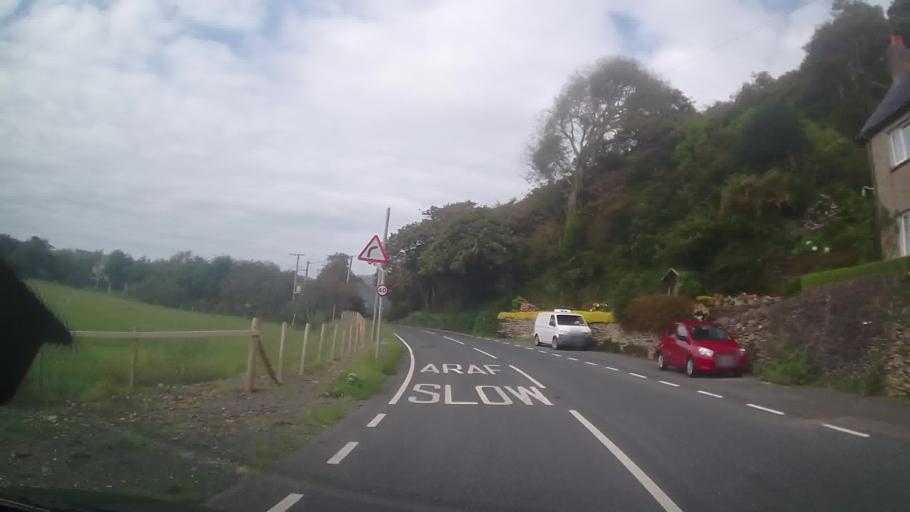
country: GB
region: Wales
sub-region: Gwynedd
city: Barmouth
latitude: 52.6966
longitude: -4.0450
